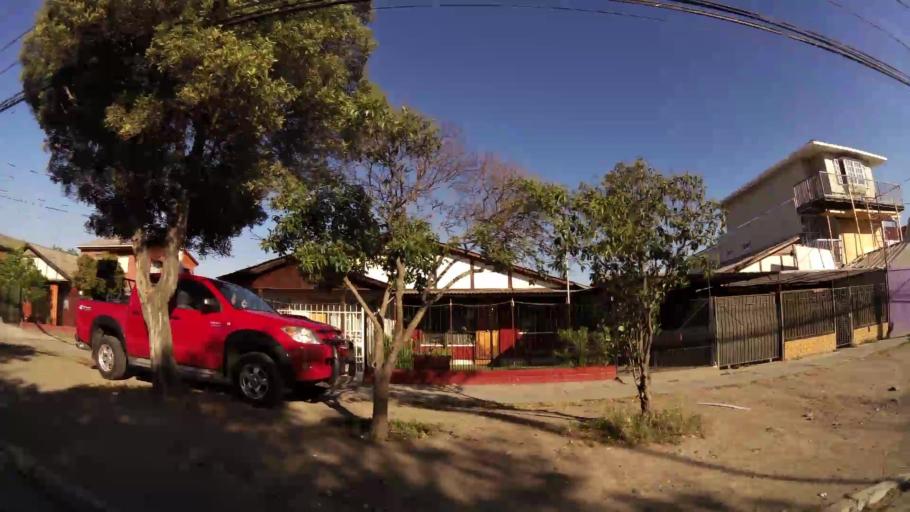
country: CL
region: Santiago Metropolitan
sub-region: Provincia de Maipo
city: San Bernardo
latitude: -33.5430
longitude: -70.7724
